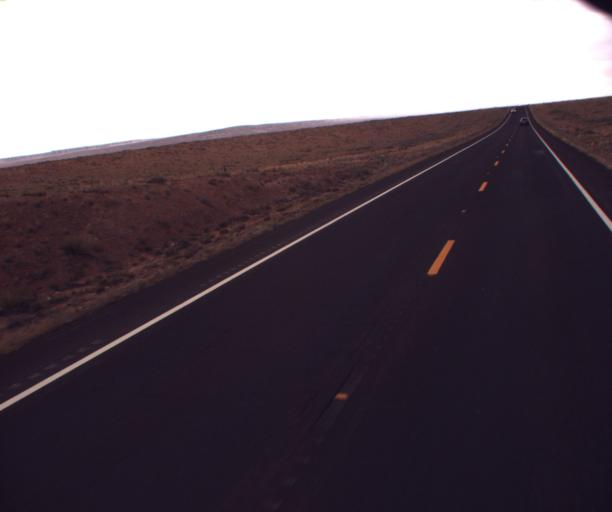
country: US
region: Arizona
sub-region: Coconino County
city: Tuba City
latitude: 36.1875
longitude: -111.0702
